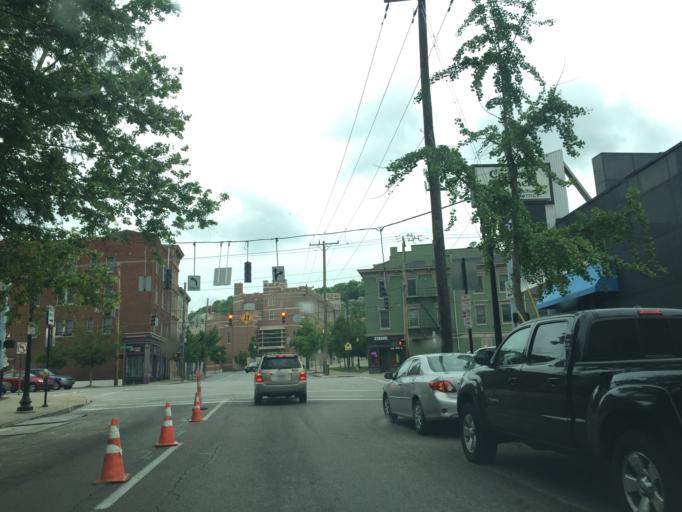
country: US
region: Kentucky
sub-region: Campbell County
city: Newport
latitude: 39.1122
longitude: -84.5124
